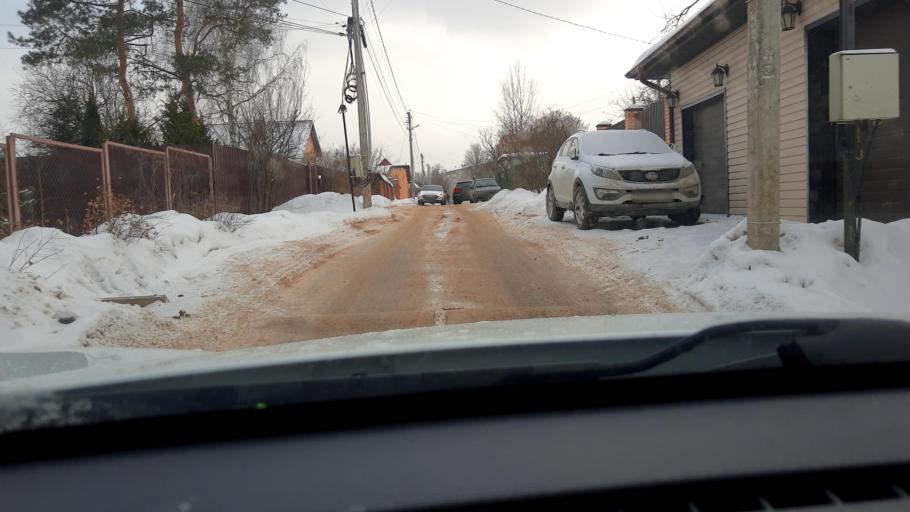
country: RU
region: Moskovskaya
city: Pavlovskaya Sloboda
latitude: 55.8217
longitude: 37.0939
